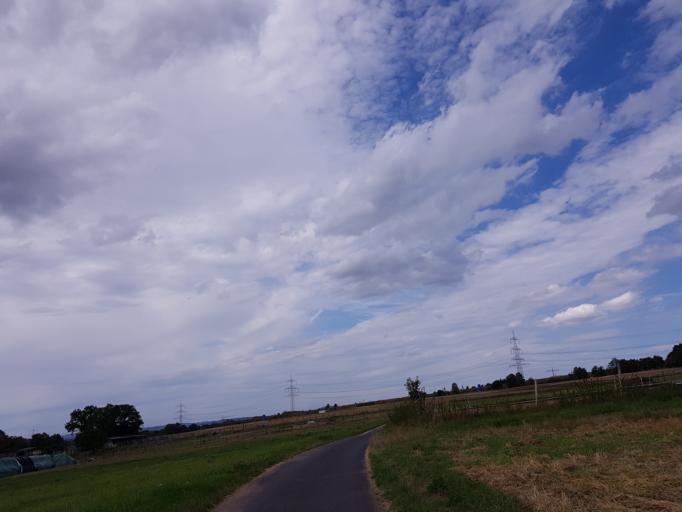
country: DE
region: Hesse
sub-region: Regierungsbezirk Giessen
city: Langgons
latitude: 50.5136
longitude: 8.6623
